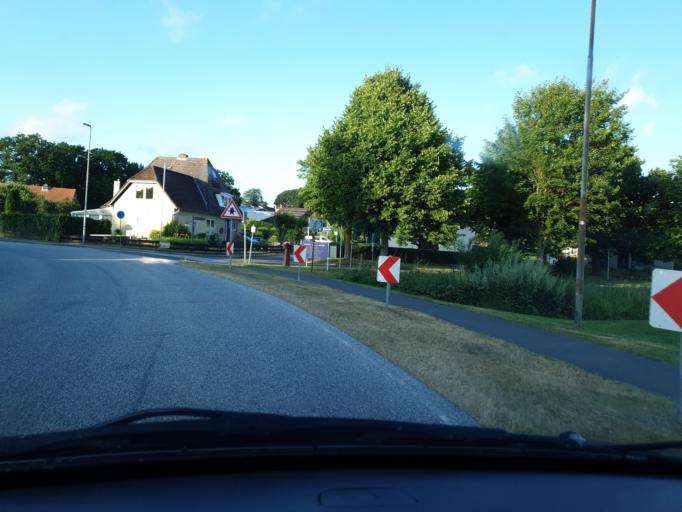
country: DE
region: Schleswig-Holstein
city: Wohrden
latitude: 54.1644
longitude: 8.9945
